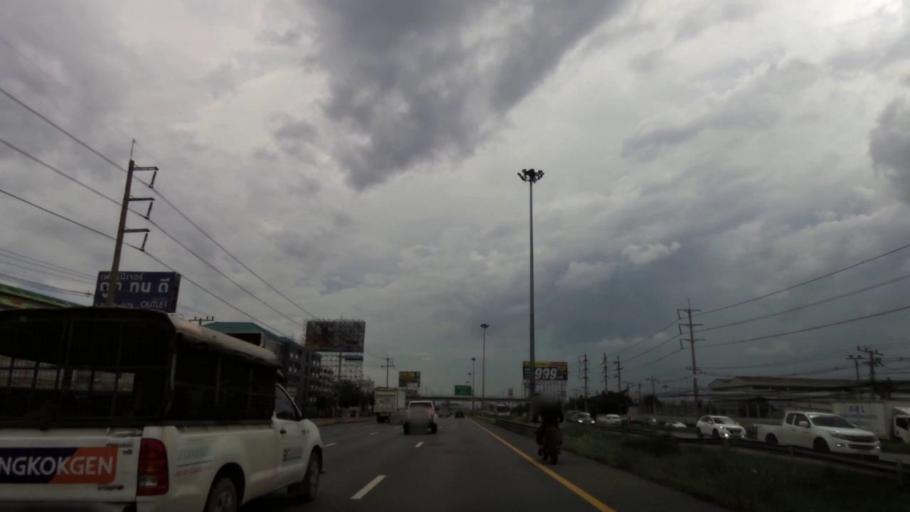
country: TH
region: Pathum Thani
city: Khlong Luang
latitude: 14.1111
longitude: 100.6187
